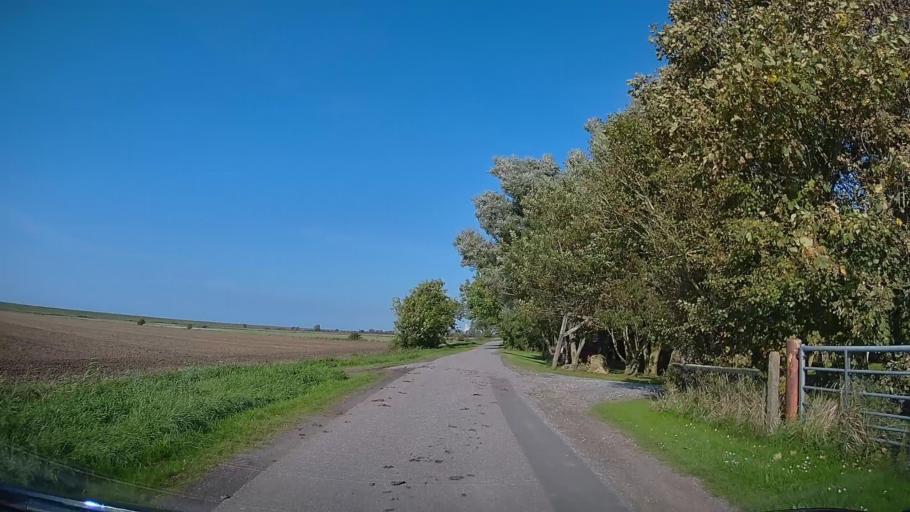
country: DE
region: Lower Saxony
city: Misselwarden
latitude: 53.6999
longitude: 8.4969
